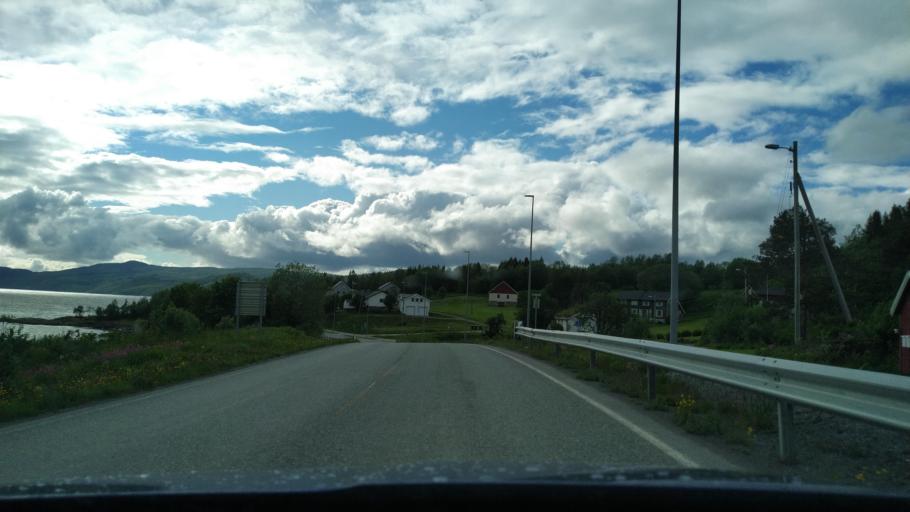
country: NO
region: Troms
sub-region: Sorreisa
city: Sorreisa
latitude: 69.1785
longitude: 18.0702
